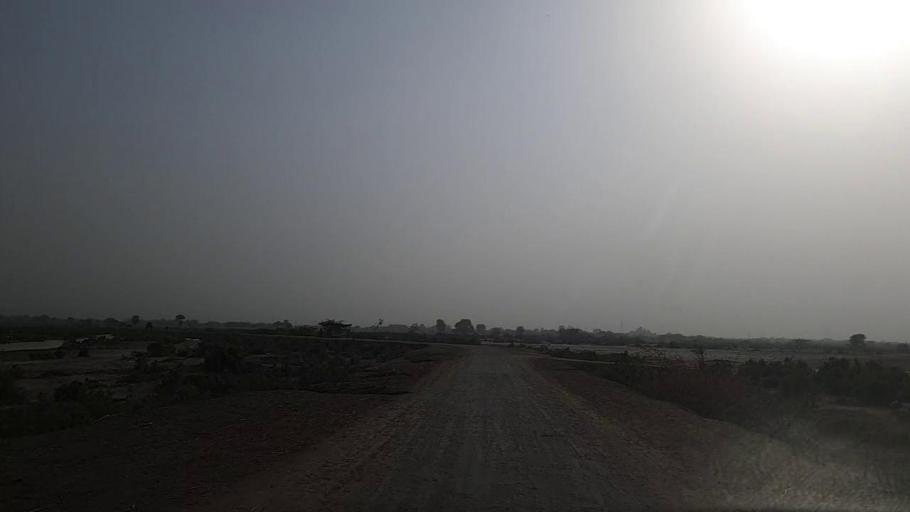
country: PK
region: Sindh
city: Pithoro
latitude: 25.4062
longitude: 69.2642
